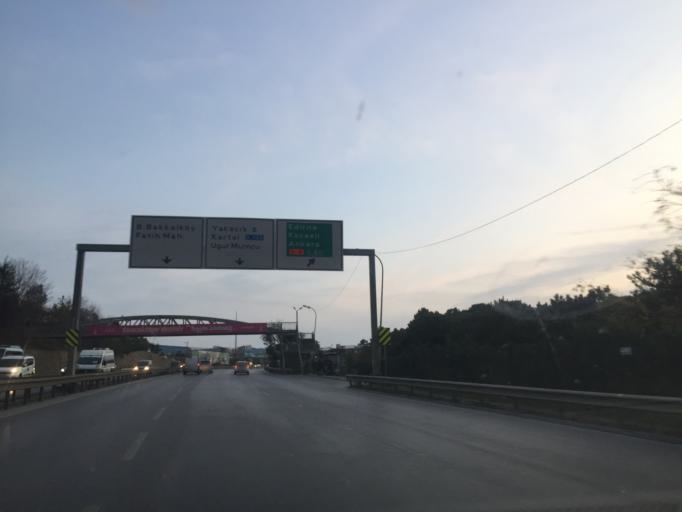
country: TR
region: Istanbul
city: Samandira
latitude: 40.9726
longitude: 29.2193
